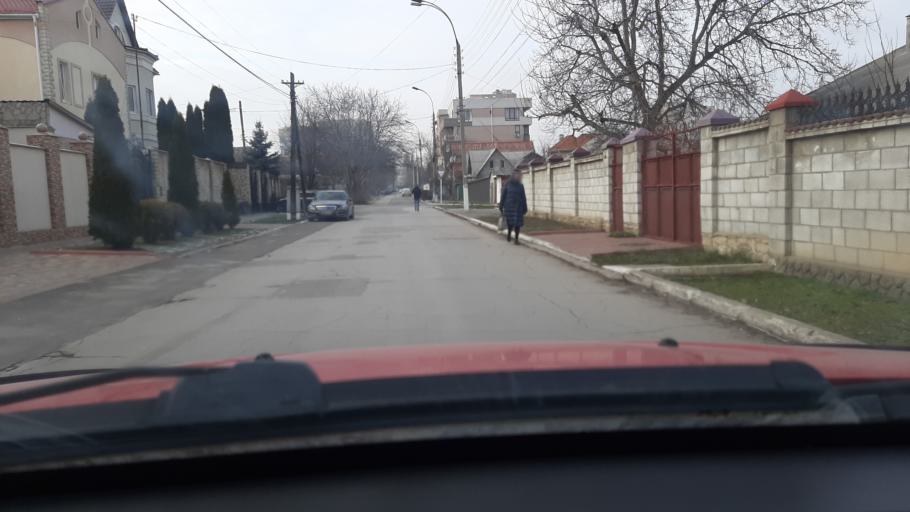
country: MD
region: Chisinau
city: Vatra
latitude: 47.0337
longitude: 28.7896
